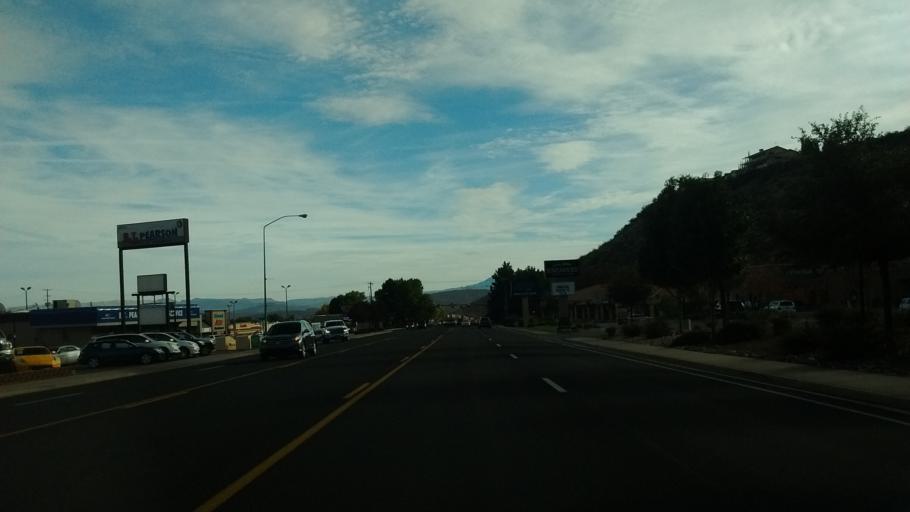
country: US
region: Utah
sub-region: Washington County
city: Saint George
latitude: 37.1123
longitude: -113.5950
